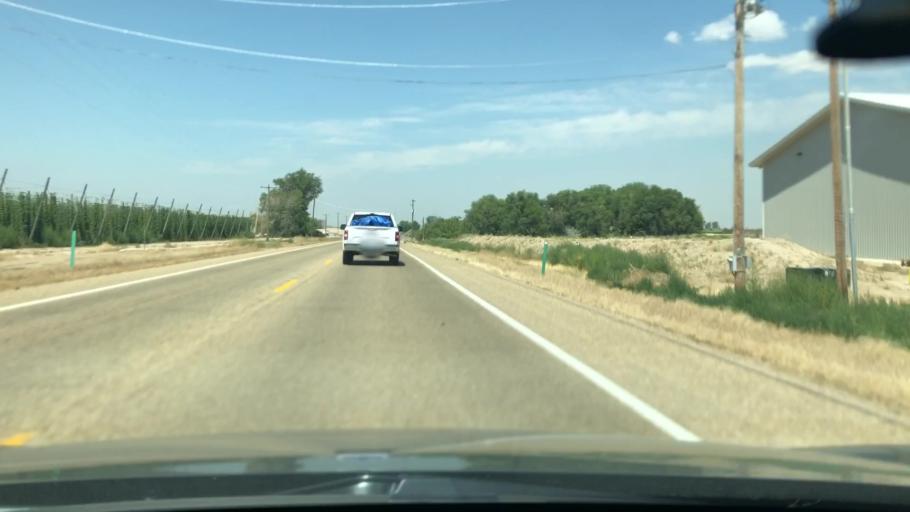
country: US
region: Idaho
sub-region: Canyon County
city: Wilder
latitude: 43.7065
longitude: -116.9119
